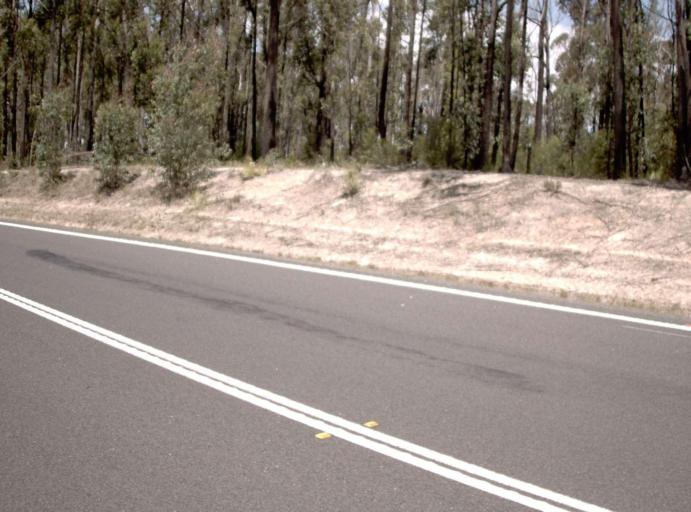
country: AU
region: New South Wales
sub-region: Bombala
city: Bombala
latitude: -37.5673
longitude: 149.1114
